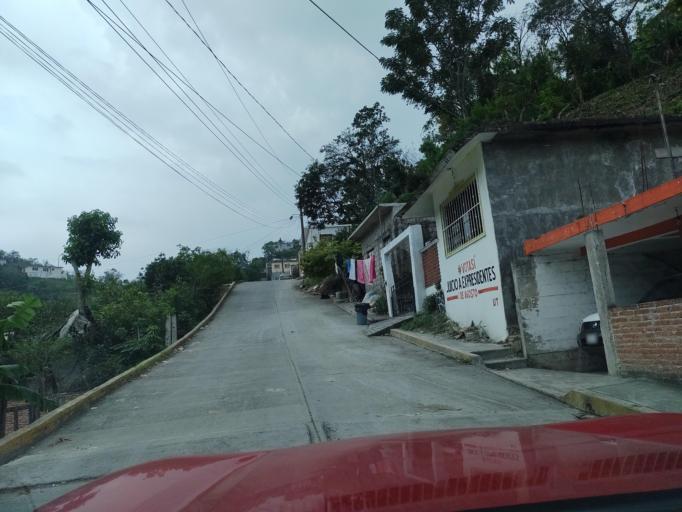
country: MX
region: Veracruz
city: Papantla de Olarte
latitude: 20.4601
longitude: -97.3307
